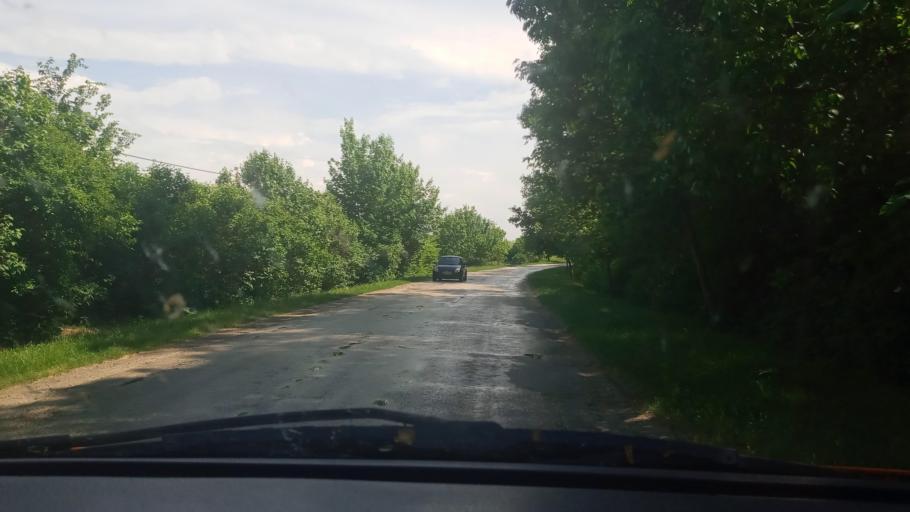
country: HU
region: Baranya
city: Siklos
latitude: 45.7978
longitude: 18.3493
